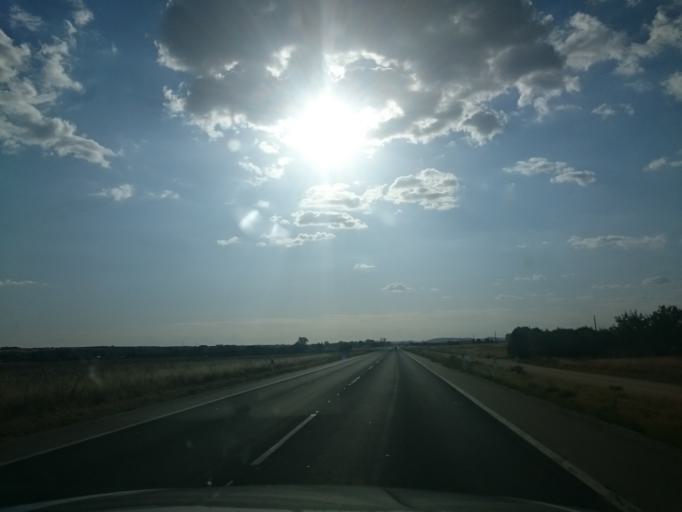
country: ES
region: Castille and Leon
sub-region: Provincia de Burgos
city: Los Tomillares
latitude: 42.3367
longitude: -3.5855
